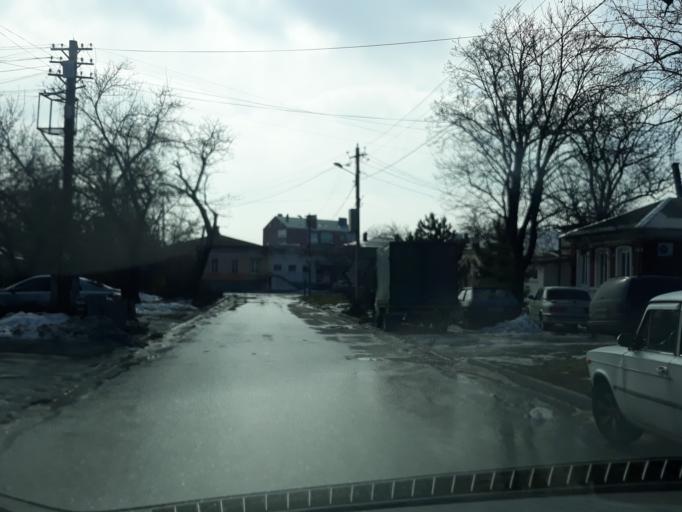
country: RU
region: Rostov
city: Taganrog
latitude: 47.2055
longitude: 38.9287
